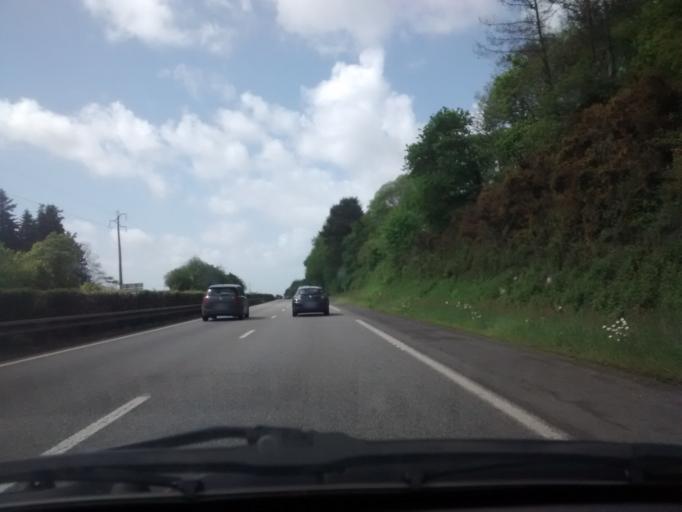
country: FR
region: Brittany
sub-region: Departement du Morbihan
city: Saint-Nolff
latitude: 47.6887
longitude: -2.6434
